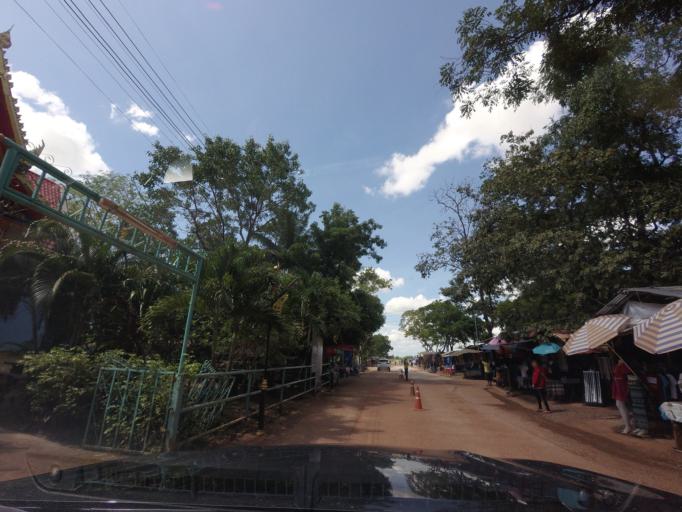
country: TH
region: Changwat Udon Thani
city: Ban Dung
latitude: 17.7434
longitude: 103.3584
